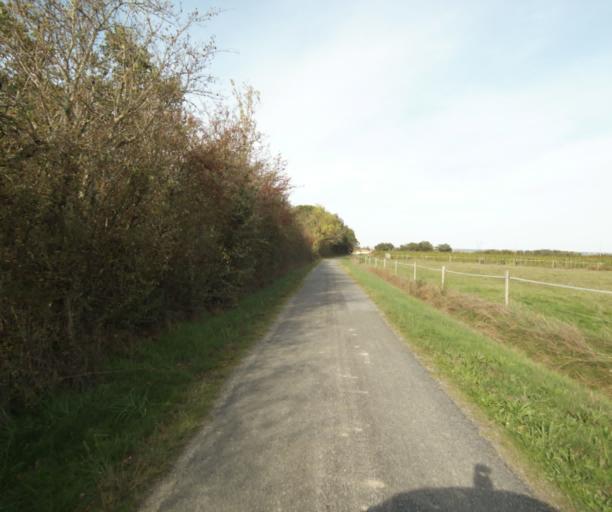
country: FR
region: Midi-Pyrenees
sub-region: Departement du Tarn-et-Garonne
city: Campsas
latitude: 43.9226
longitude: 1.3249
